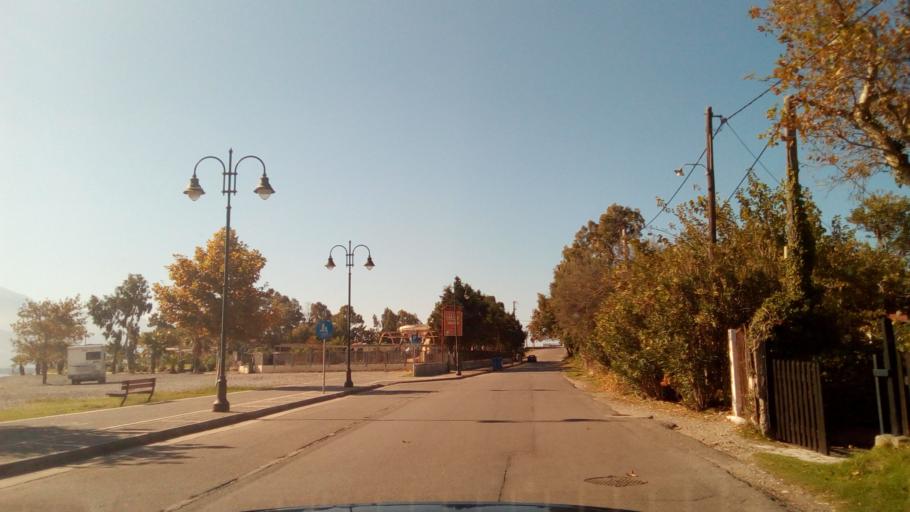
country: GR
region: West Greece
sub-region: Nomos Aitolias kai Akarnanias
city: Nafpaktos
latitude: 38.3846
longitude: 21.8192
